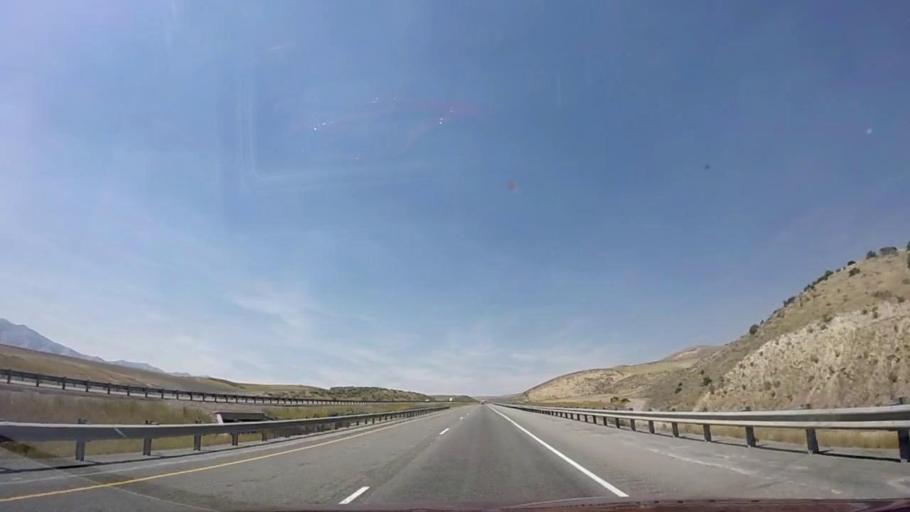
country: US
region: Idaho
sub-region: Power County
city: American Falls
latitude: 42.1741
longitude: -113.0051
